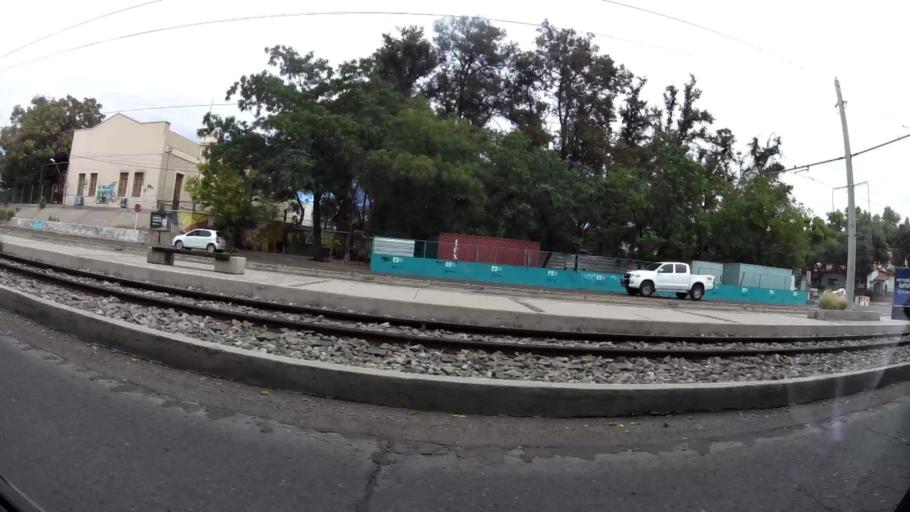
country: AR
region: Mendoza
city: Mendoza
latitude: -32.8938
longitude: -68.8509
